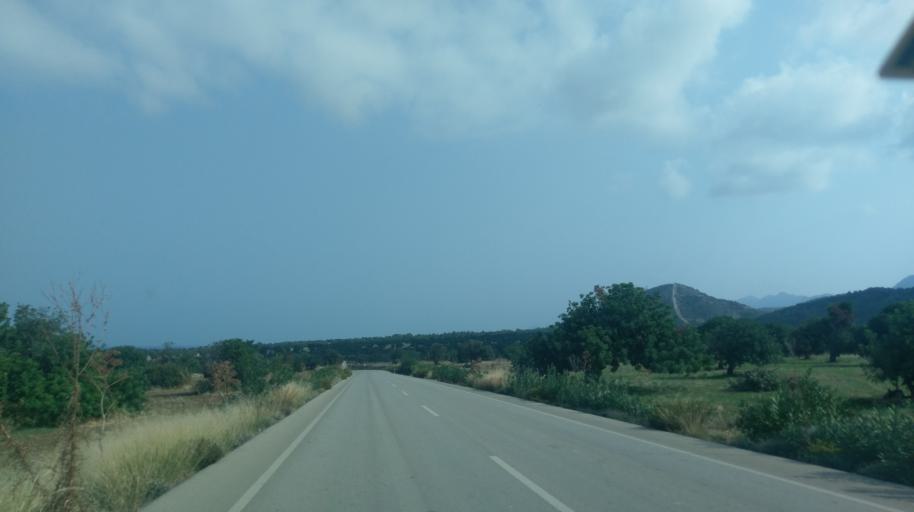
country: CY
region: Ammochostos
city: Lefkonoiko
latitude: 35.3957
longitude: 33.7561
